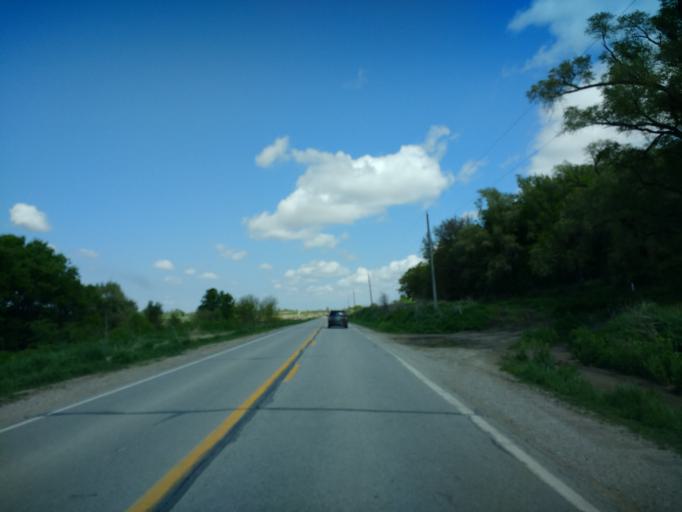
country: US
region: Iowa
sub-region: Harrison County
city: Missouri Valley
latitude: 41.4849
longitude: -95.8857
